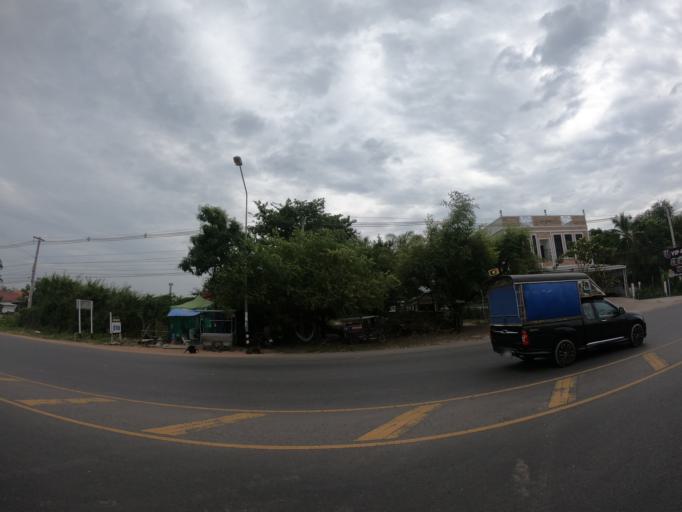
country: TH
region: Roi Et
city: Roi Et
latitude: 16.0643
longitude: 103.6677
